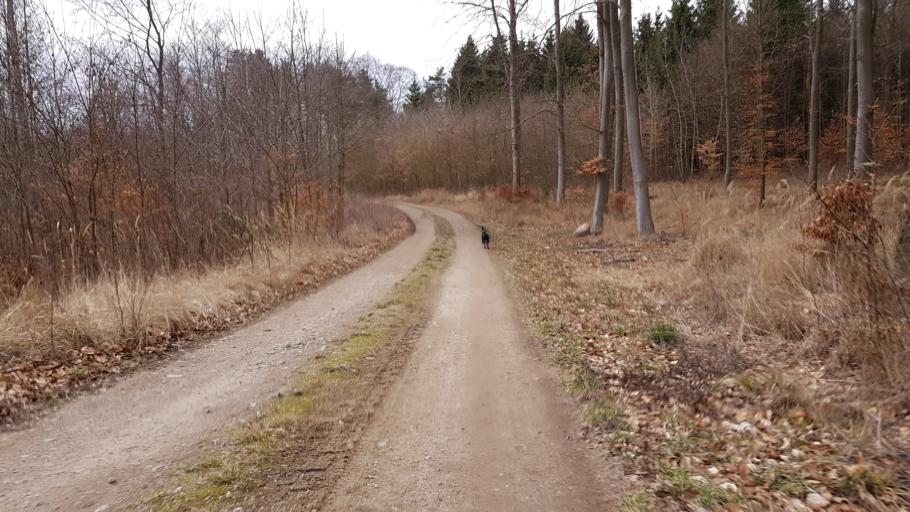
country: PL
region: West Pomeranian Voivodeship
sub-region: Powiat pyrzycki
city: Kozielice
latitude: 53.0843
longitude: 14.7471
